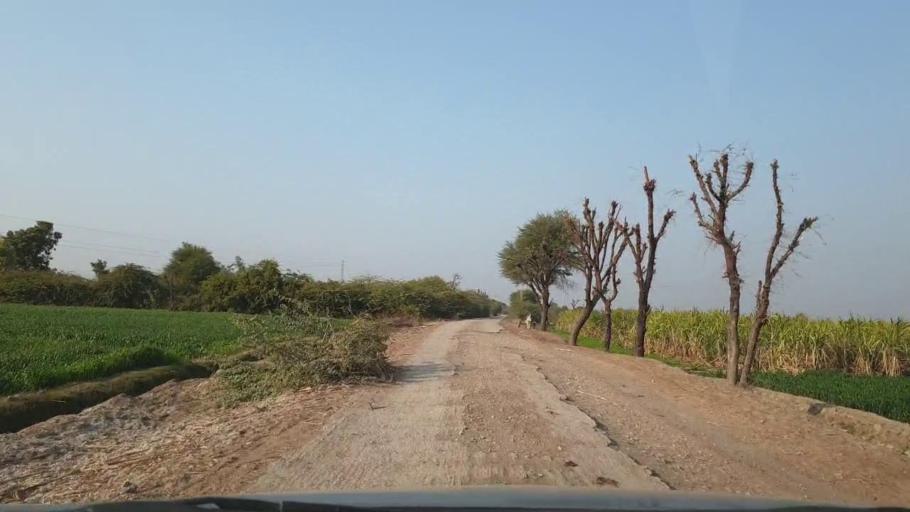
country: PK
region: Sindh
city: Tando Adam
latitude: 25.6850
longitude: 68.6328
